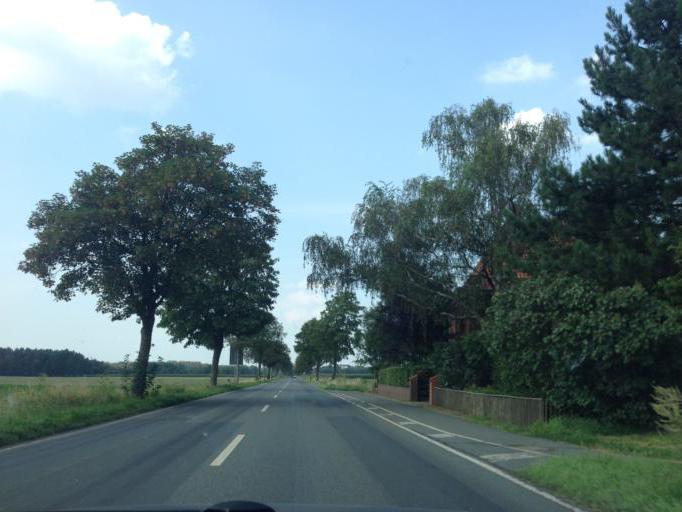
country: DE
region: Lower Saxony
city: Edemissen
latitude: 52.3605
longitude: 10.2490
